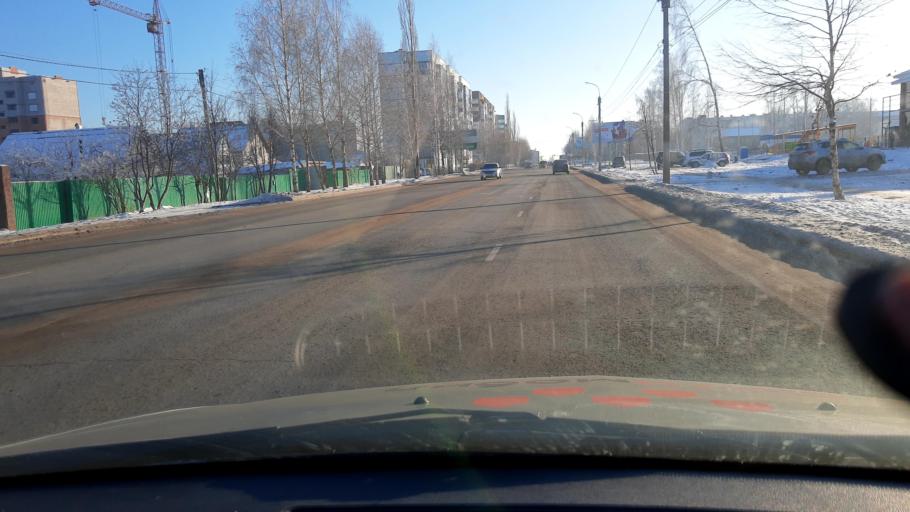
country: RU
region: Bashkortostan
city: Blagoveshchensk
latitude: 55.0534
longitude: 55.9506
